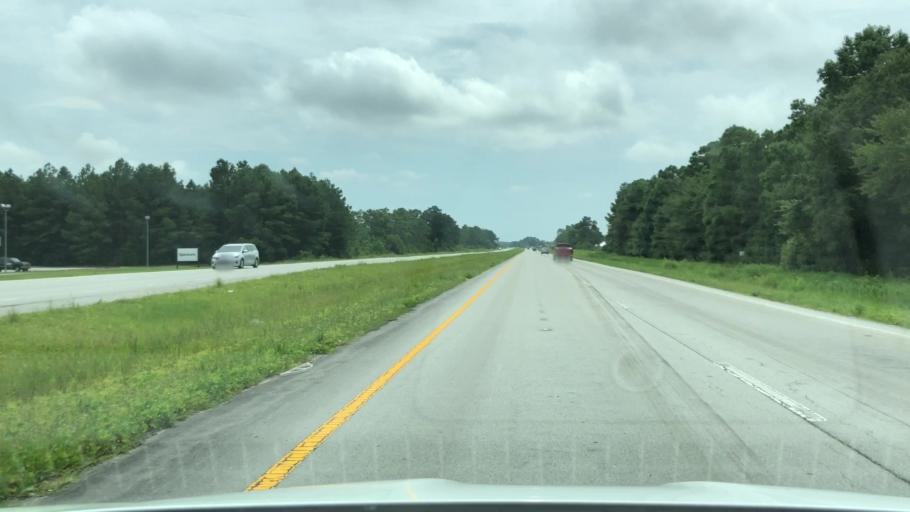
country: US
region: North Carolina
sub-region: Carteret County
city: Newport
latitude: 34.8018
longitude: -76.8785
